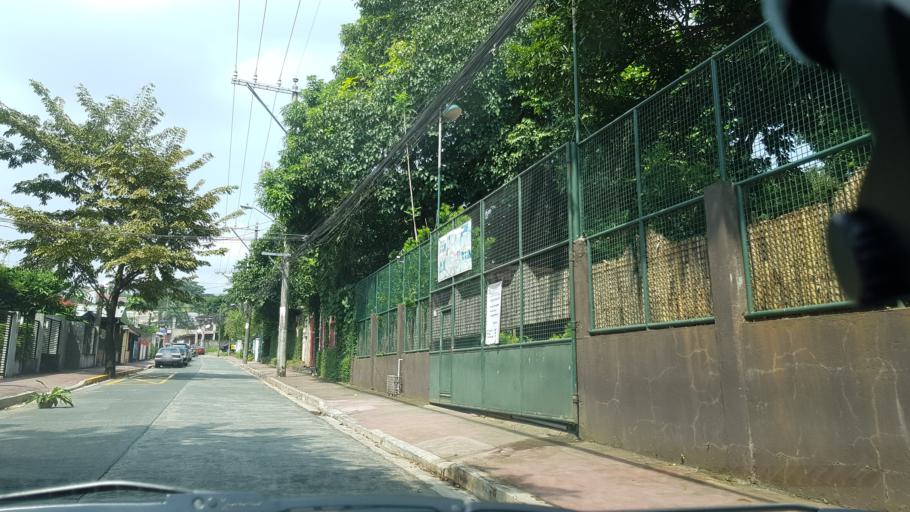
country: PH
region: Calabarzon
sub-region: Province of Rizal
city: Antipolo
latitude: 14.6508
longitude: 121.1198
